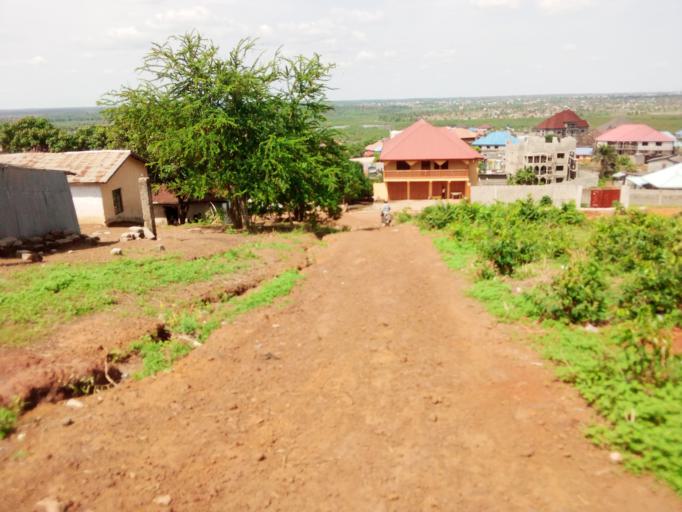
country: SL
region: Western Area
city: Waterloo
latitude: 8.3508
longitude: -13.0796
